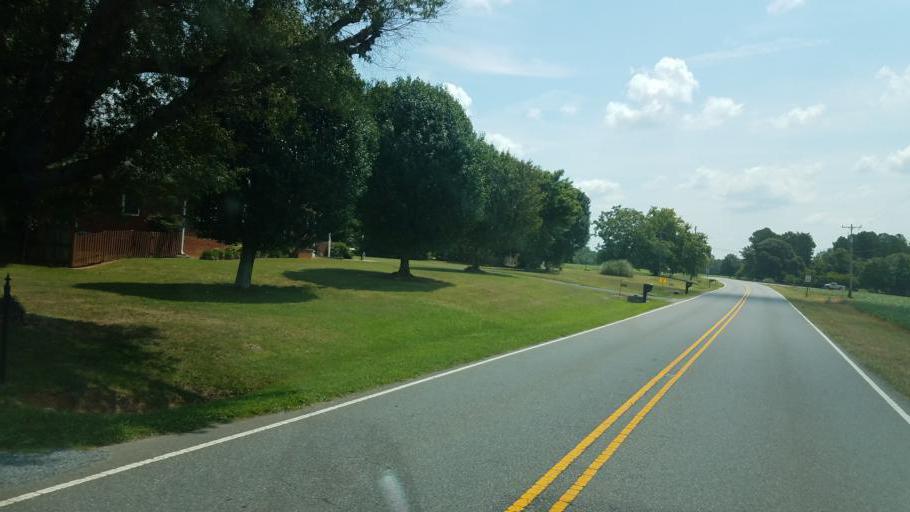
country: US
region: North Carolina
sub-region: Cleveland County
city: Kings Mountain
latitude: 35.2670
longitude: -81.3454
